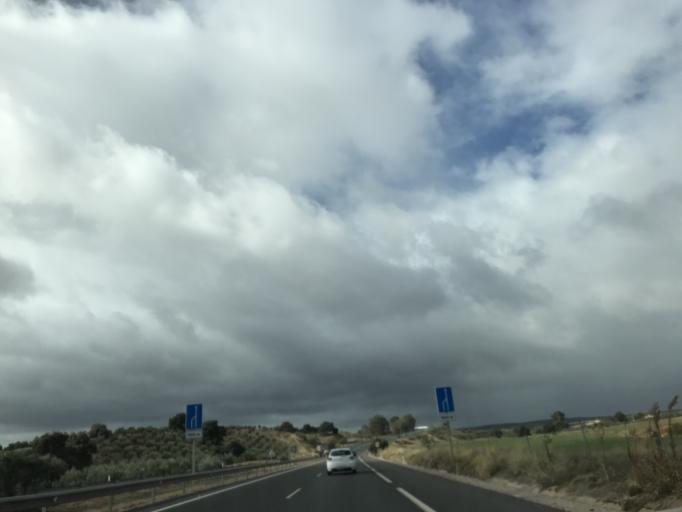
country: ES
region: Andalusia
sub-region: Provincia de Jaen
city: Bailen
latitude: 38.0981
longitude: -3.7308
